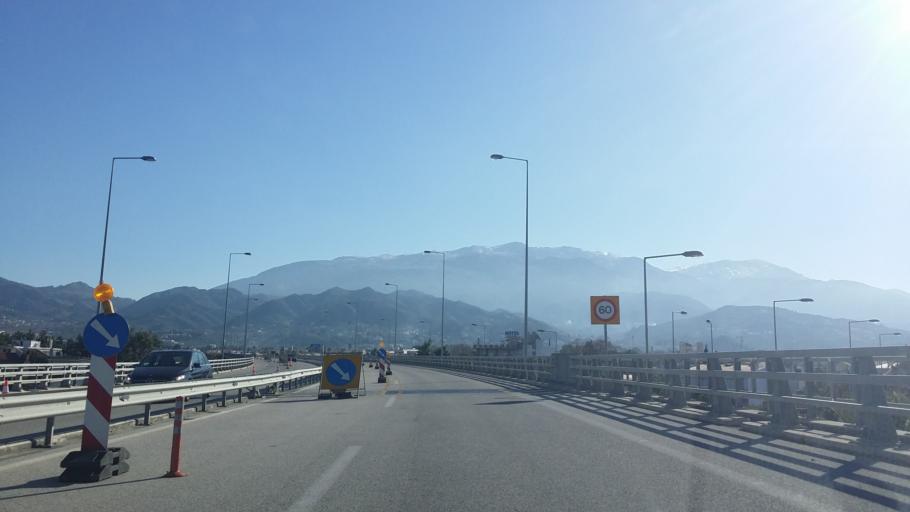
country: GR
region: West Greece
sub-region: Nomos Achaias
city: Rio
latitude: 38.3062
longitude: 21.7818
